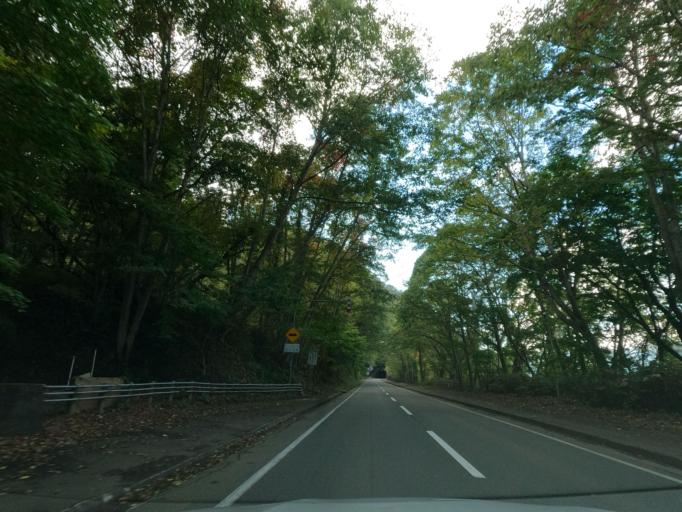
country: JP
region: Hokkaido
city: Shiraoi
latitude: 42.7042
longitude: 141.2945
